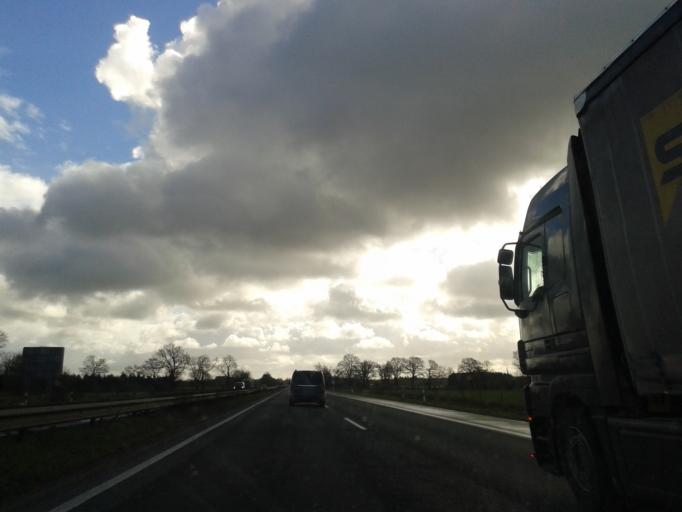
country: DE
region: Lower Saxony
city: Wiefelstede
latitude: 53.1803
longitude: 8.1110
